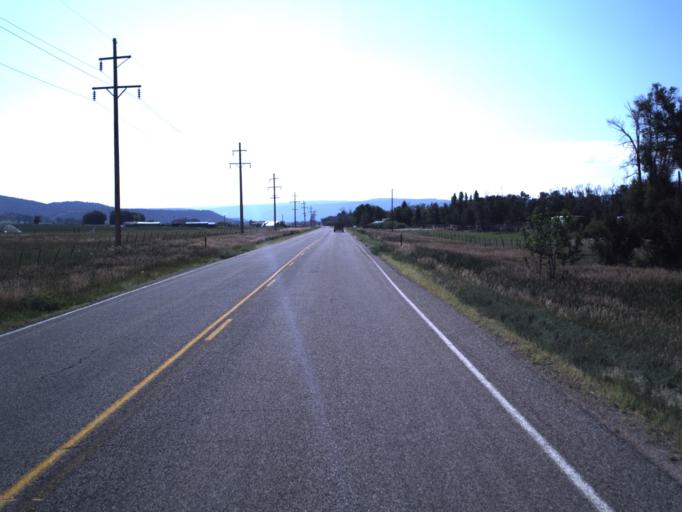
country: US
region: Utah
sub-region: Duchesne County
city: Duchesne
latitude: 40.3857
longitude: -110.7436
